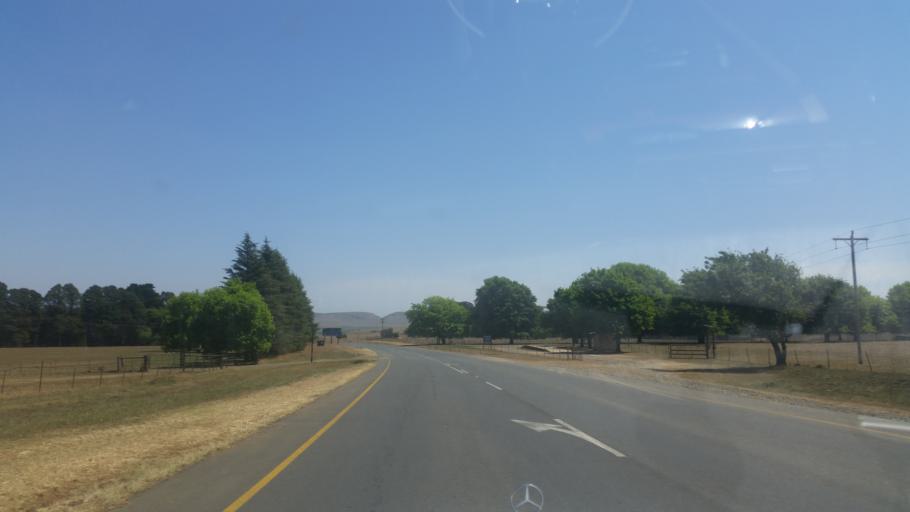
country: ZA
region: KwaZulu-Natal
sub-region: uMgungundlovu District Municipality
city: Mooirivier
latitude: -29.1483
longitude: 29.9767
